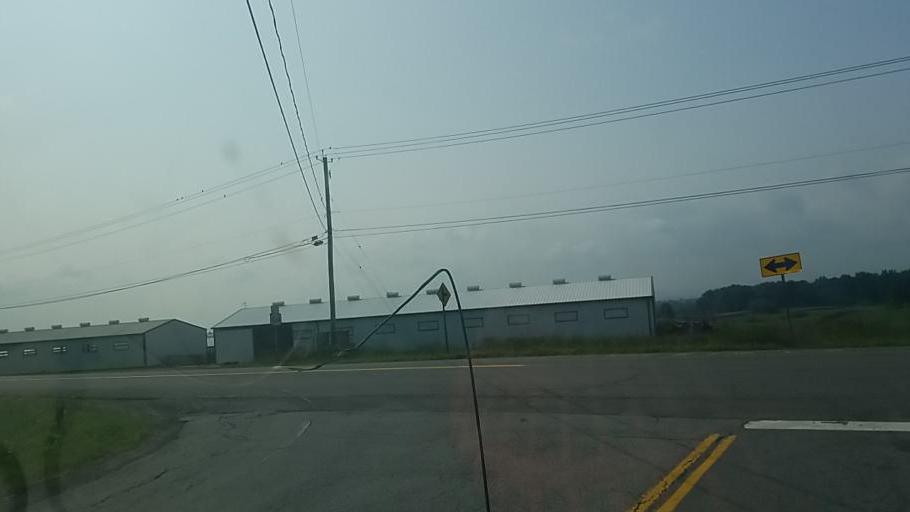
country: US
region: New York
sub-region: Fulton County
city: Johnstown
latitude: 43.0017
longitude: -74.4083
